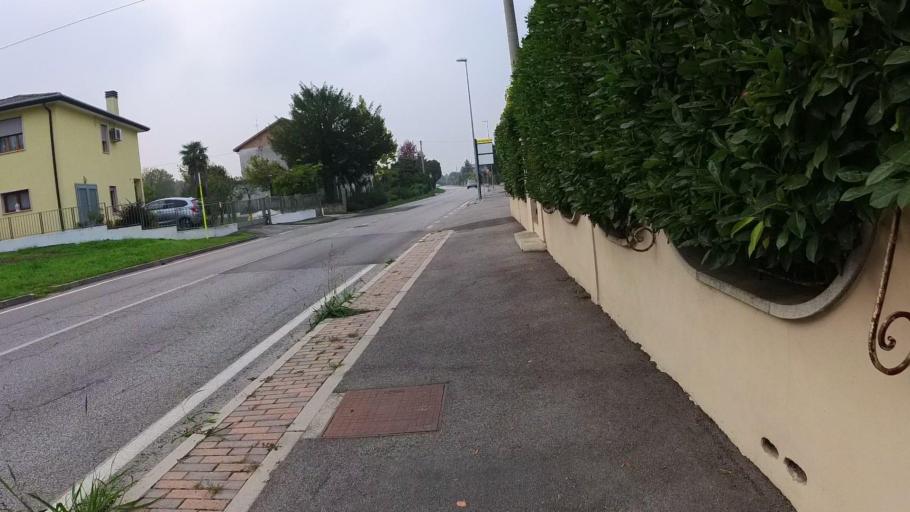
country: IT
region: Veneto
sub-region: Provincia di Venezia
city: Fosso
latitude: 45.3832
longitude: 12.0571
